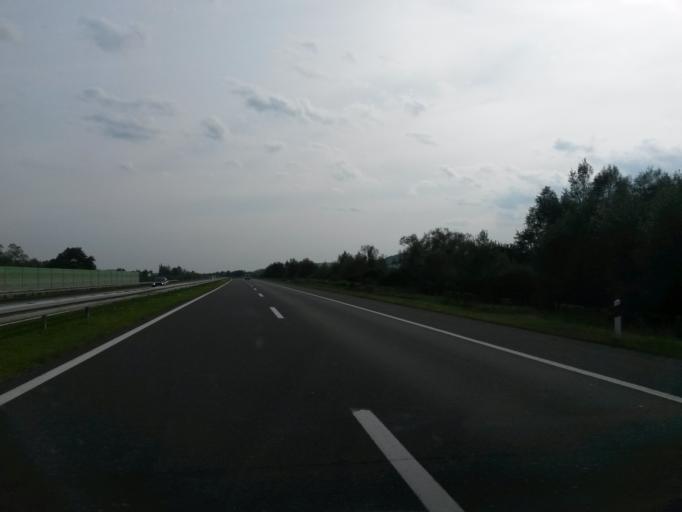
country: HR
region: Varazdinska
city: Remetinec
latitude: 46.0593
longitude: 16.2977
